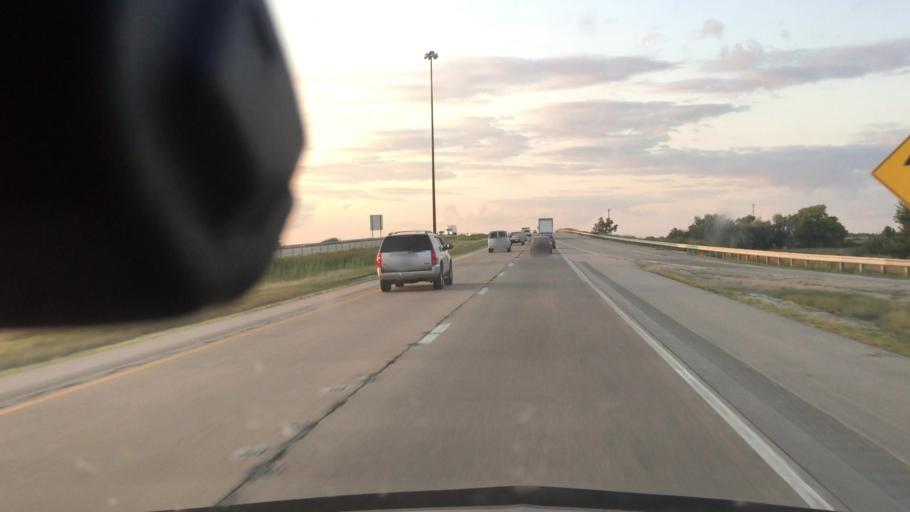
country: US
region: Illinois
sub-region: Livingston County
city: Dwight
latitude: 41.0968
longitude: -88.4498
